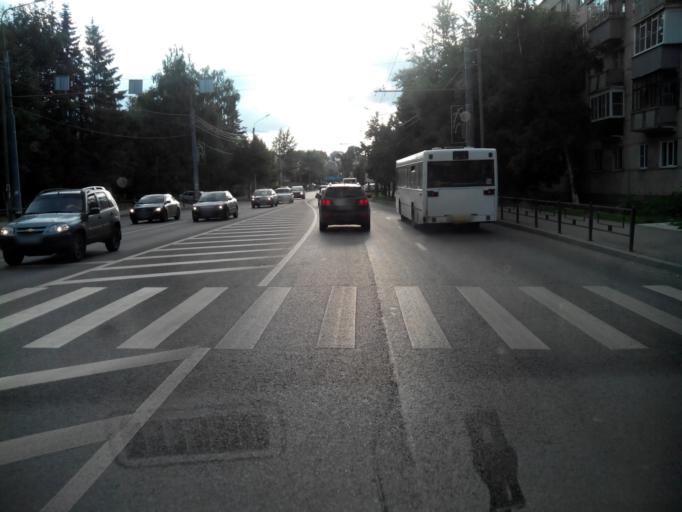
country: RU
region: Penza
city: Penza
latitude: 53.2043
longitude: 44.9842
